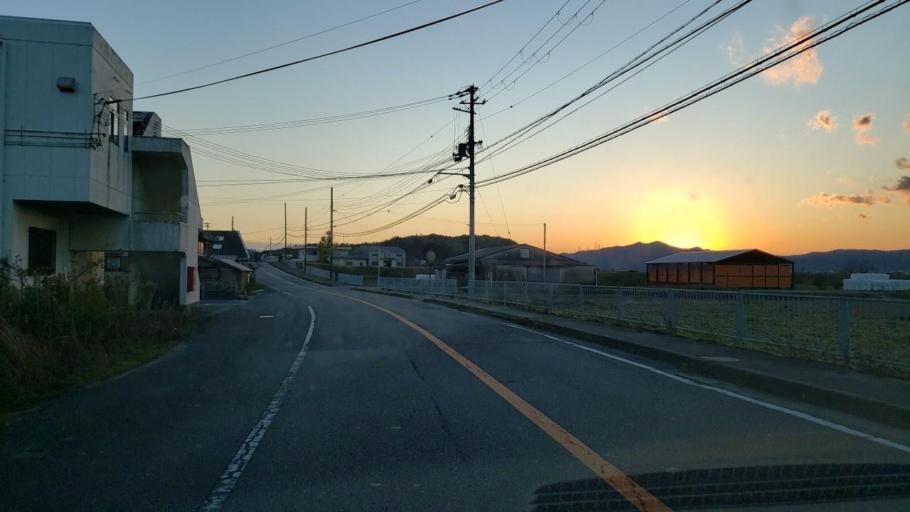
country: JP
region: Hyogo
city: Fukura
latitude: 34.3306
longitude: 134.7752
